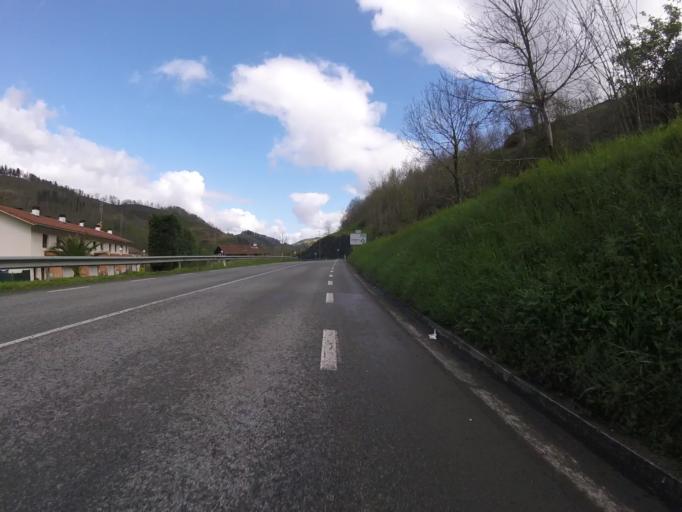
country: ES
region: Basque Country
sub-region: Provincia de Guipuzcoa
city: Amezqueta
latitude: 43.0516
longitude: -2.0883
